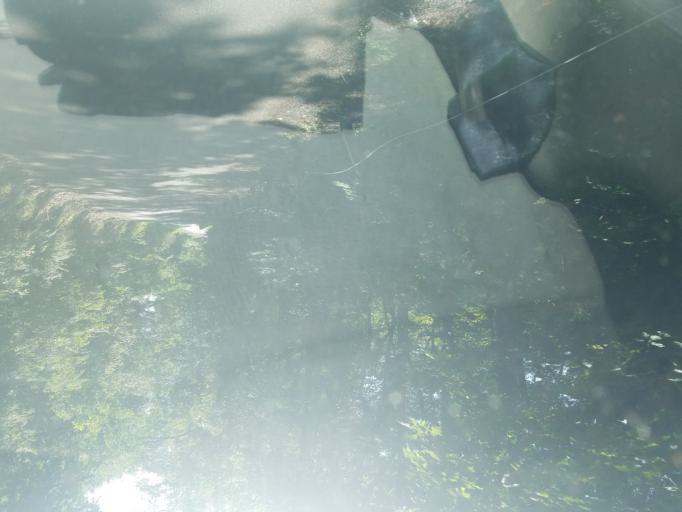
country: US
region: Pennsylvania
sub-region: Clarion County
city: Clarion
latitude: 41.1759
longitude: -79.4302
